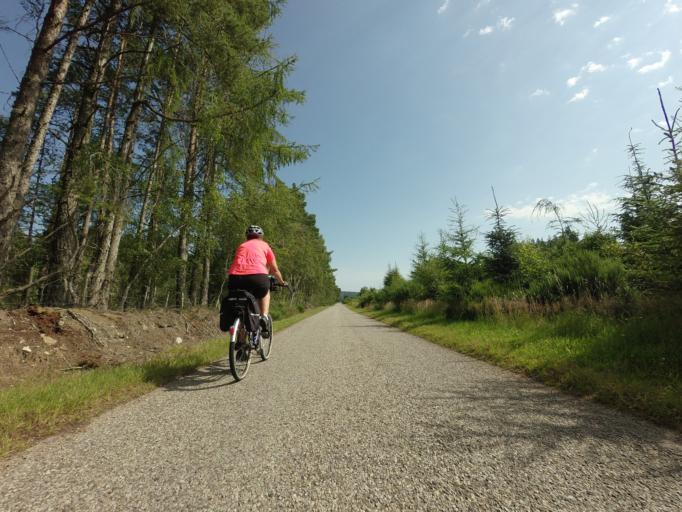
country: GB
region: Scotland
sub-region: Highland
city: Invergordon
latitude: 57.7396
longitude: -4.1832
